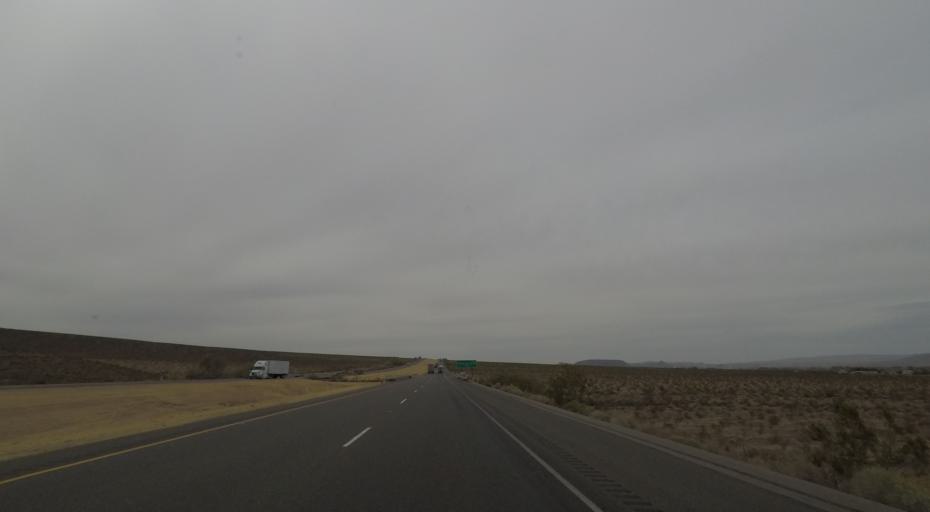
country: US
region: California
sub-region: San Bernardino County
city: Barstow
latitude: 34.8382
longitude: -116.7783
